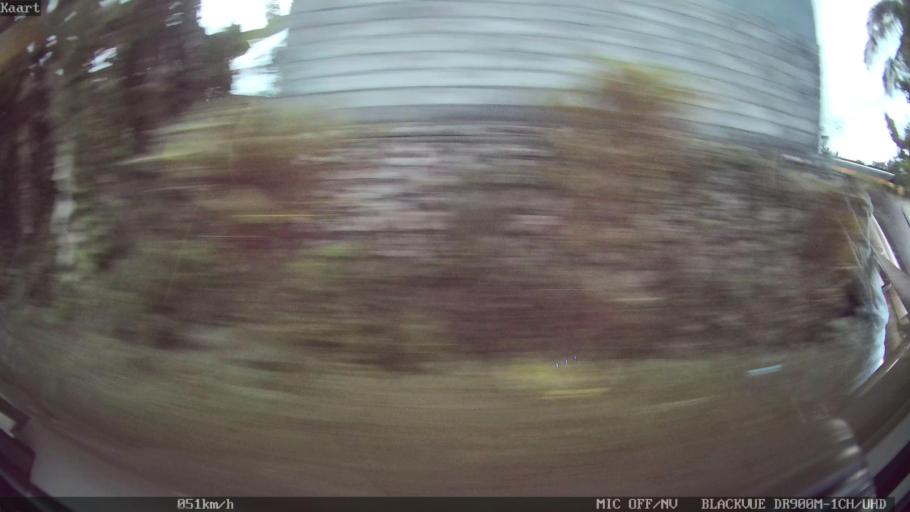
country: ID
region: Bali
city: Empalan
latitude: -8.4051
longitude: 115.1469
